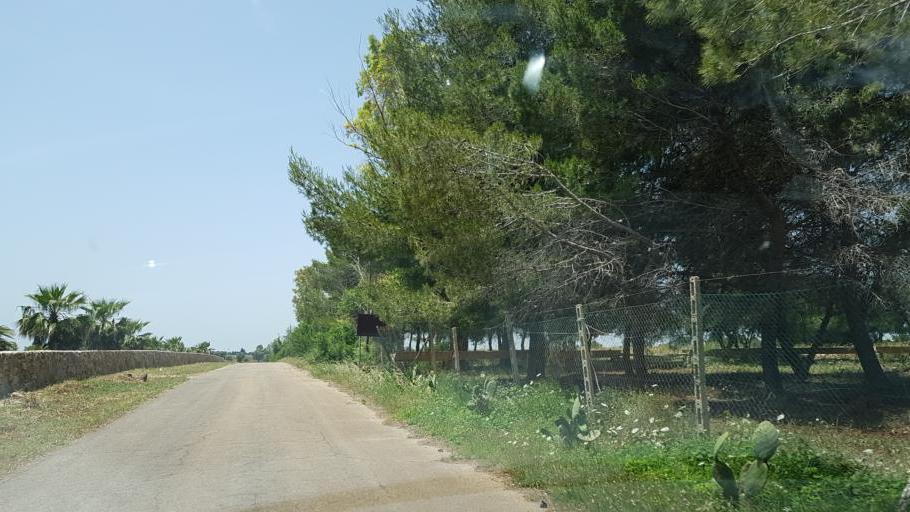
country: IT
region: Apulia
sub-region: Provincia di Lecce
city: Porto Cesareo
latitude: 40.3260
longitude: 17.8562
